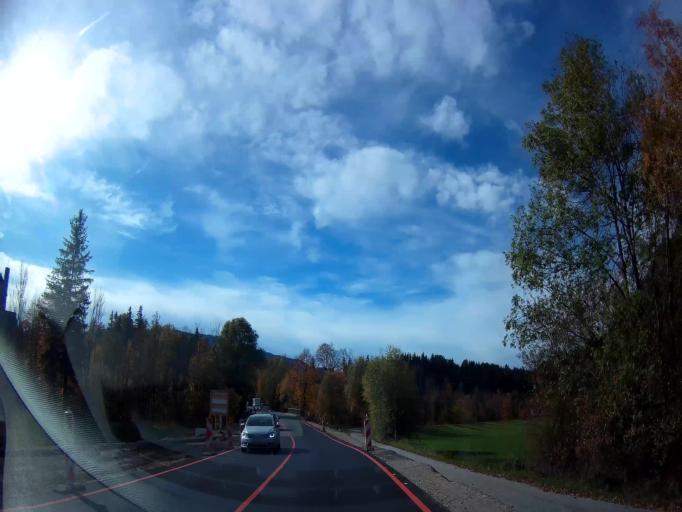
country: AT
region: Styria
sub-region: Politischer Bezirk Liezen
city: Irdning
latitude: 47.5210
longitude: 14.0799
